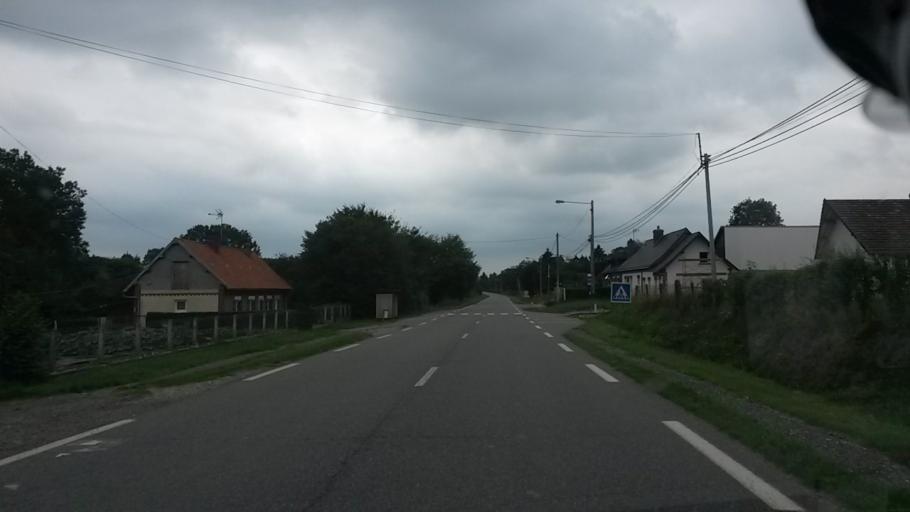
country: FR
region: Haute-Normandie
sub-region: Departement de la Seine-Maritime
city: Gaillefontaine
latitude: 49.7032
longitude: 1.6548
